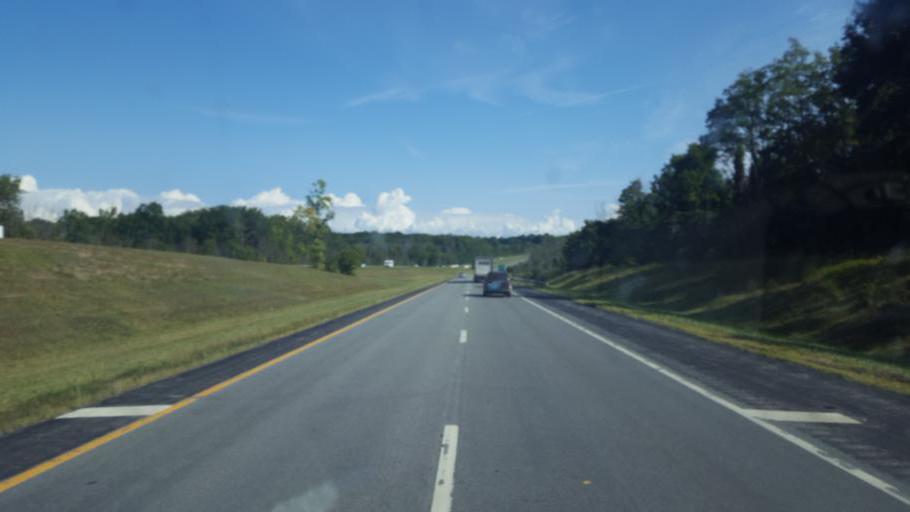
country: US
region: Ohio
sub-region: Medina County
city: Brunswick
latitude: 41.1760
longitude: -81.7604
